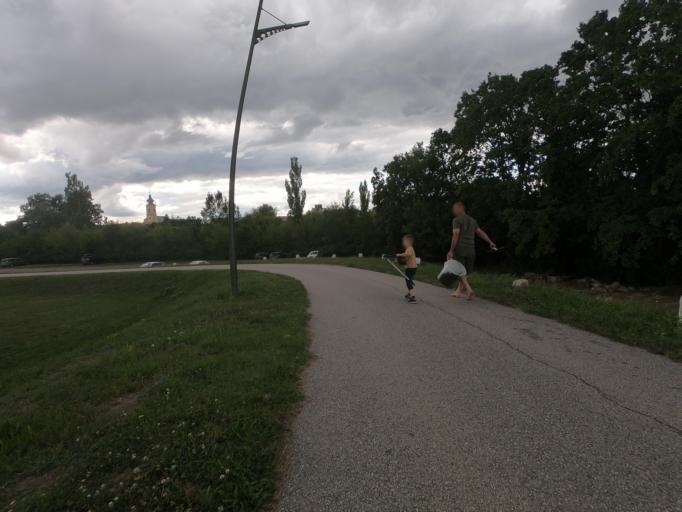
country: HU
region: Heves
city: Poroszlo
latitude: 47.6436
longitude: 20.6585
